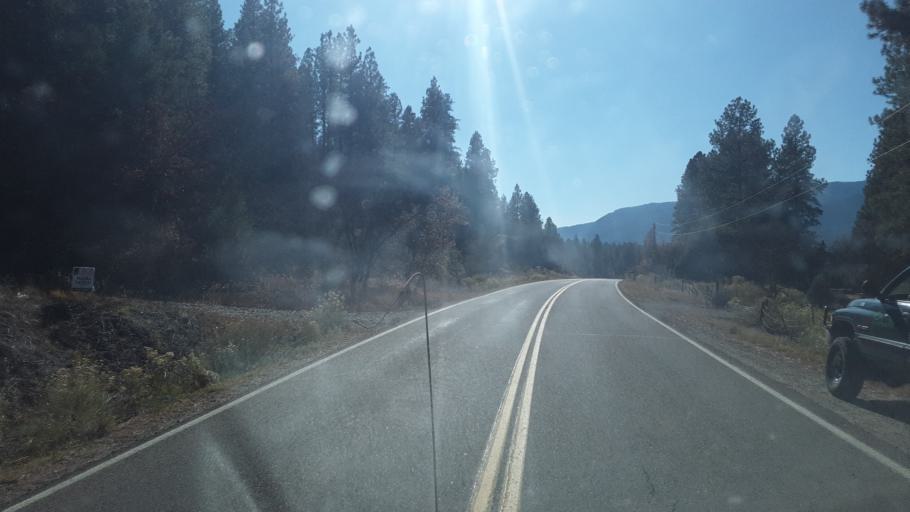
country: US
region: Colorado
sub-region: La Plata County
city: Durango
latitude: 37.4169
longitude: -107.8037
